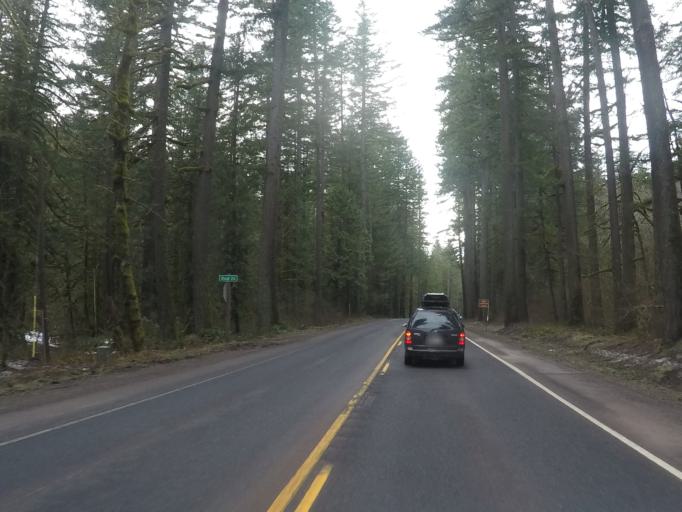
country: US
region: Oregon
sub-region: Clackamas County
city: Mount Hood Village
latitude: 45.3160
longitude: -121.8989
